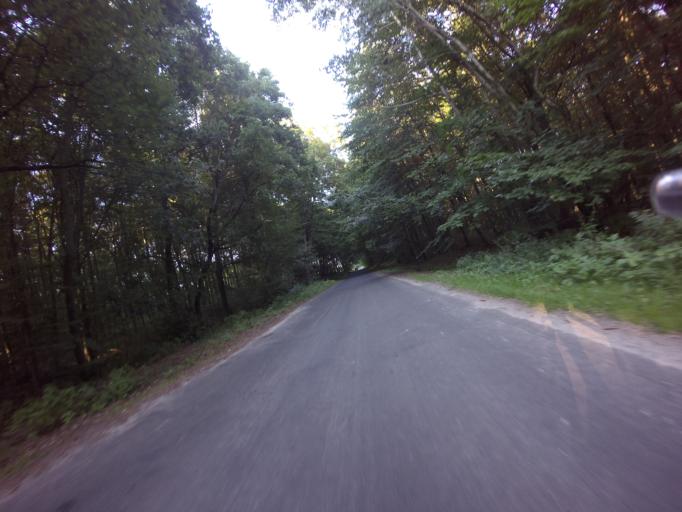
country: PL
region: West Pomeranian Voivodeship
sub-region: Powiat choszczenski
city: Choszczno
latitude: 53.2262
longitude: 15.4099
